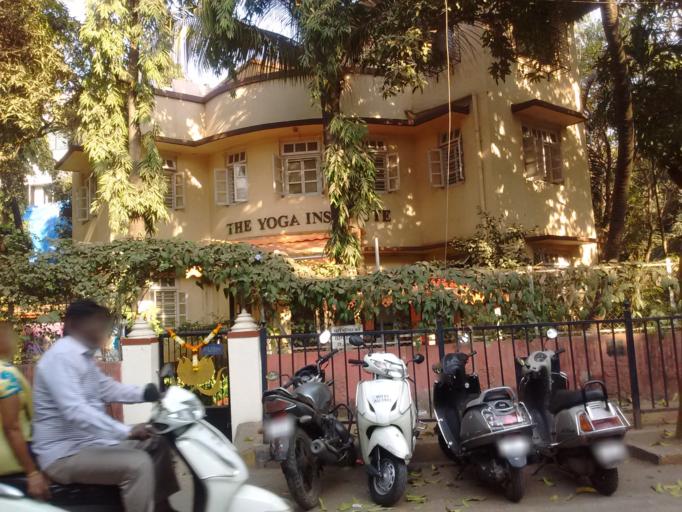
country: IN
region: Maharashtra
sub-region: Mumbai Suburban
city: Mumbai
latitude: 19.0851
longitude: 72.8431
